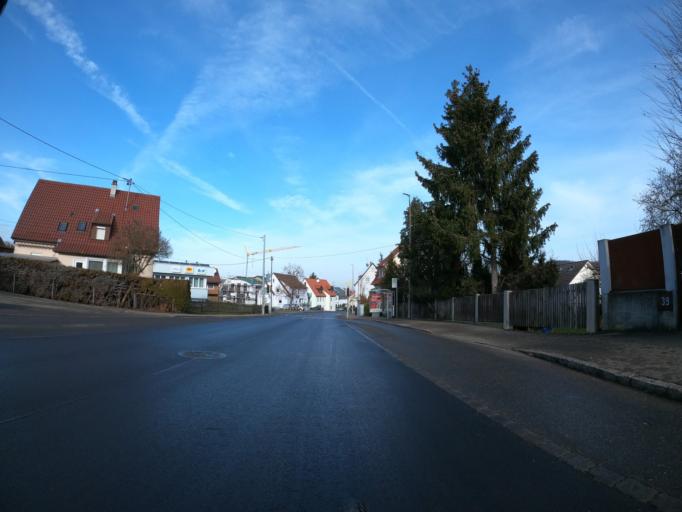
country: DE
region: Baden-Wuerttemberg
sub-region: Tuebingen Region
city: Reutlingen
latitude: 48.5167
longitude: 9.2286
